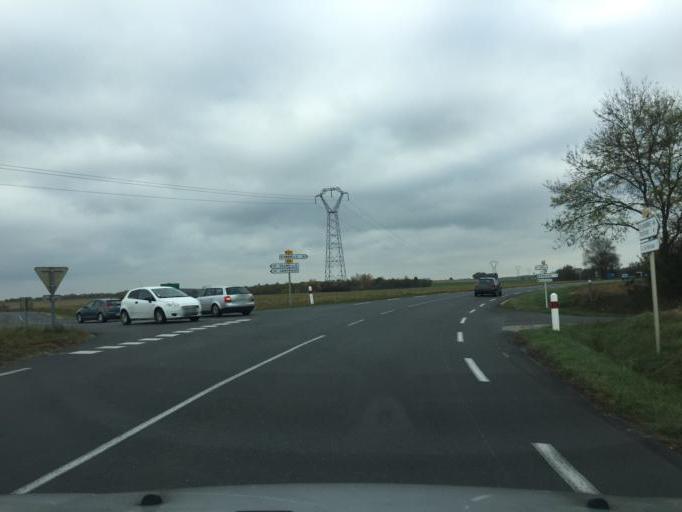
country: FR
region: Rhone-Alpes
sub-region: Departement de l'Ain
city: Reyrieux
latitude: 45.9429
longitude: 4.8291
